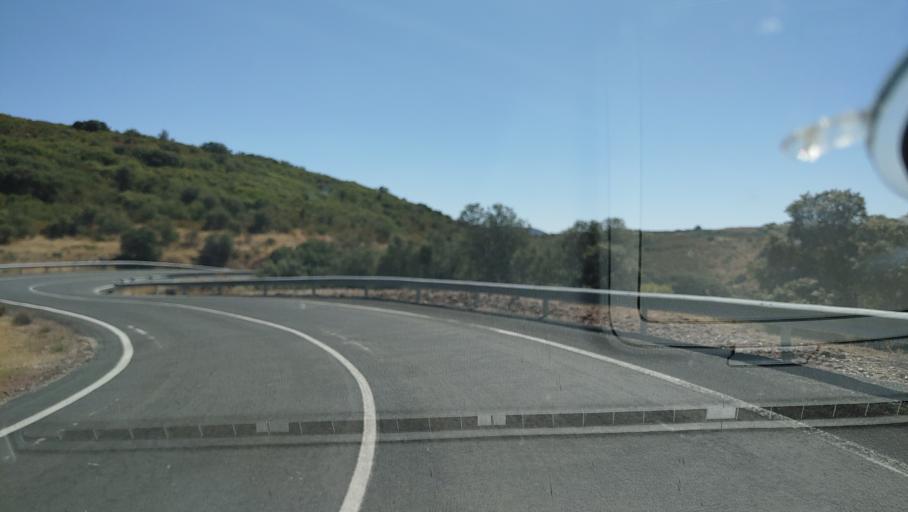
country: ES
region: Castille-La Mancha
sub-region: Provincia de Ciudad Real
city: Albaladejo
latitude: 38.5203
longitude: -2.7850
